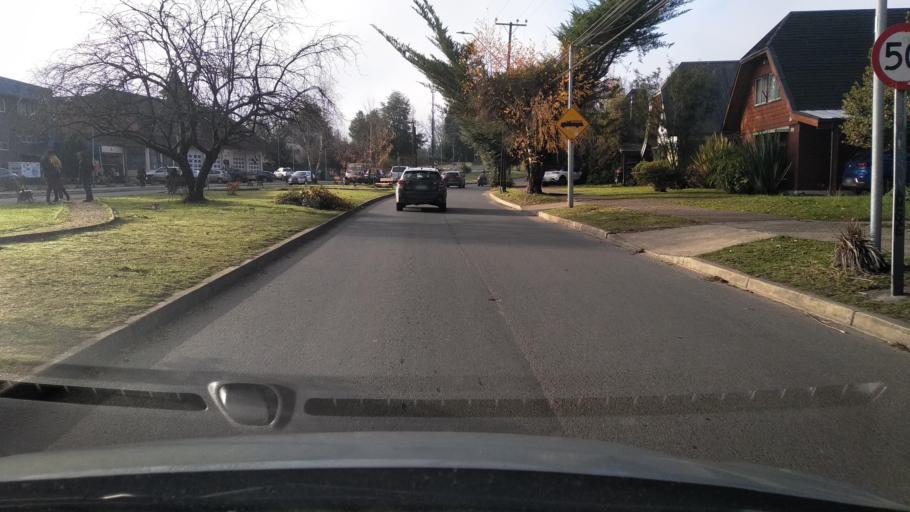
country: CL
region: Los Rios
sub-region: Provincia de Valdivia
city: Valdivia
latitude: -39.8097
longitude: -73.2573
